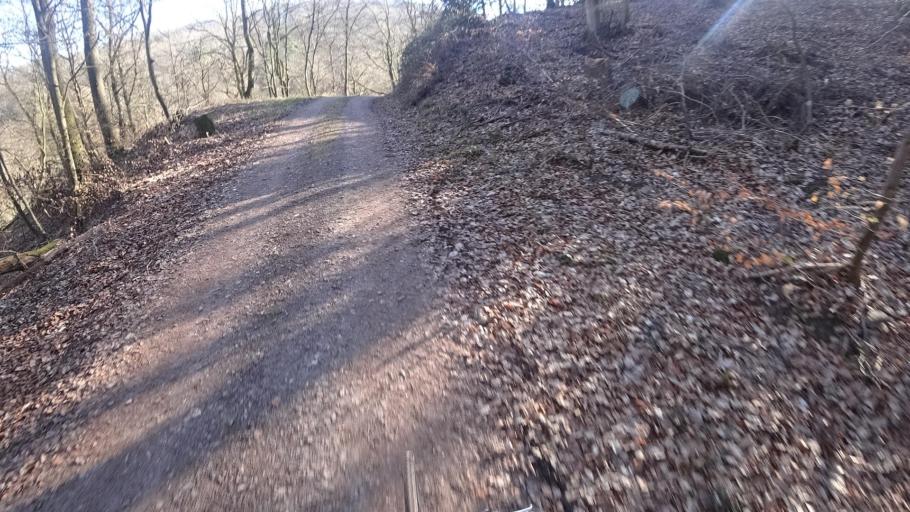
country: DE
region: Rheinland-Pfalz
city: Boppard
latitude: 50.2123
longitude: 7.5883
